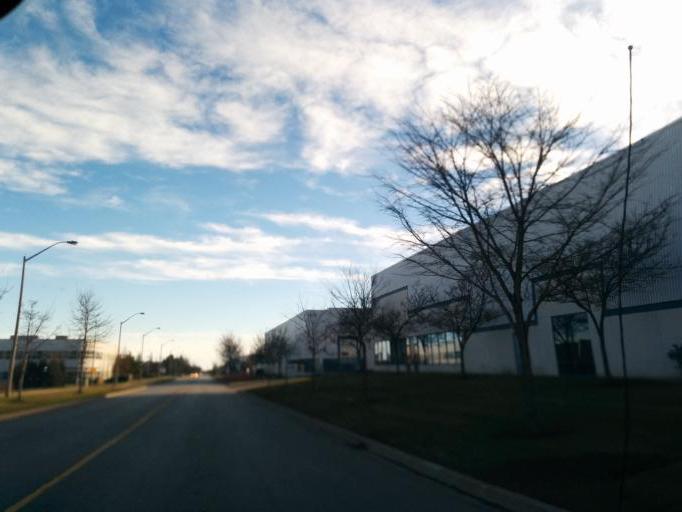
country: CA
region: Ontario
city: Oakville
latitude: 43.5092
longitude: -79.6842
